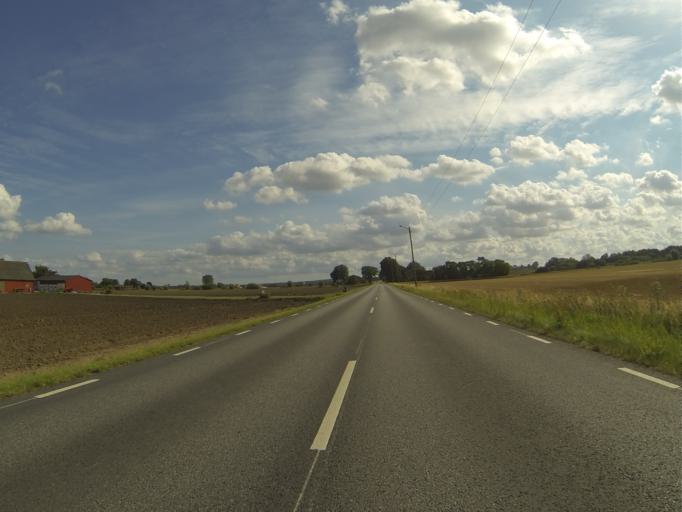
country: SE
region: Skane
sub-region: Eslovs Kommun
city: Eslov
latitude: 55.7477
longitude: 13.3253
